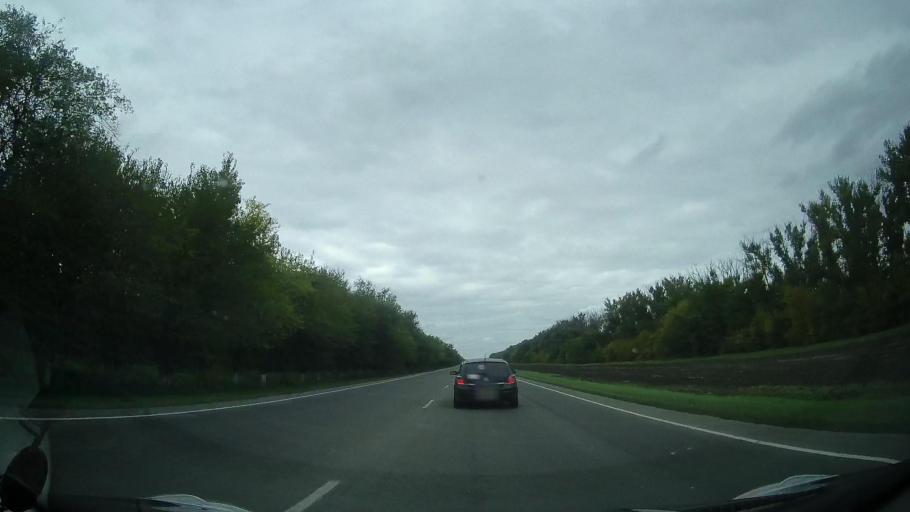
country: RU
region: Rostov
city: Yegorlykskaya
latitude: 46.6073
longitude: 40.6112
